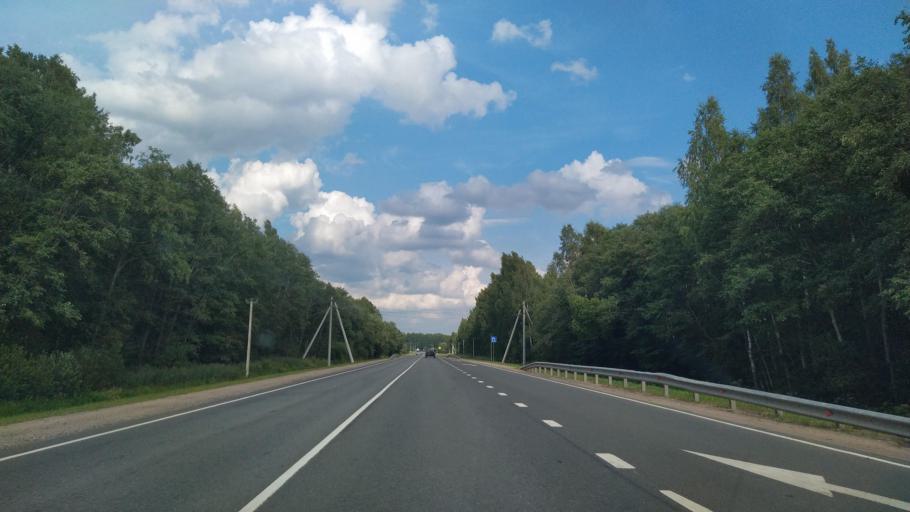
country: RU
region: Novgorod
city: Sol'tsy
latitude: 58.1742
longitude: 30.5133
